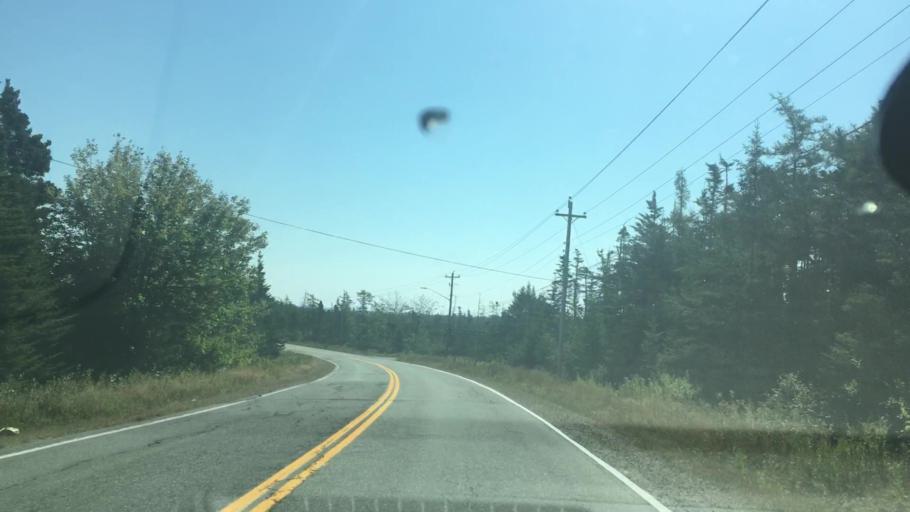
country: CA
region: Nova Scotia
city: New Glasgow
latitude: 44.9189
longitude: -62.3341
